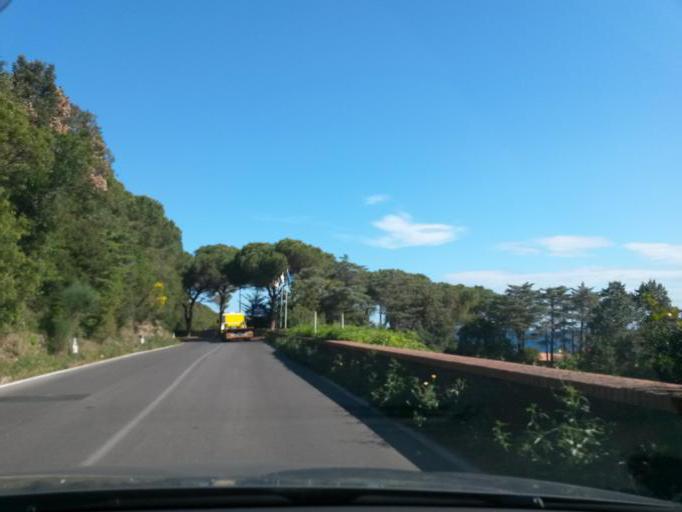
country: IT
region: Tuscany
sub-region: Provincia di Livorno
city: Marciana Marina
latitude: 42.8006
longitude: 10.2114
